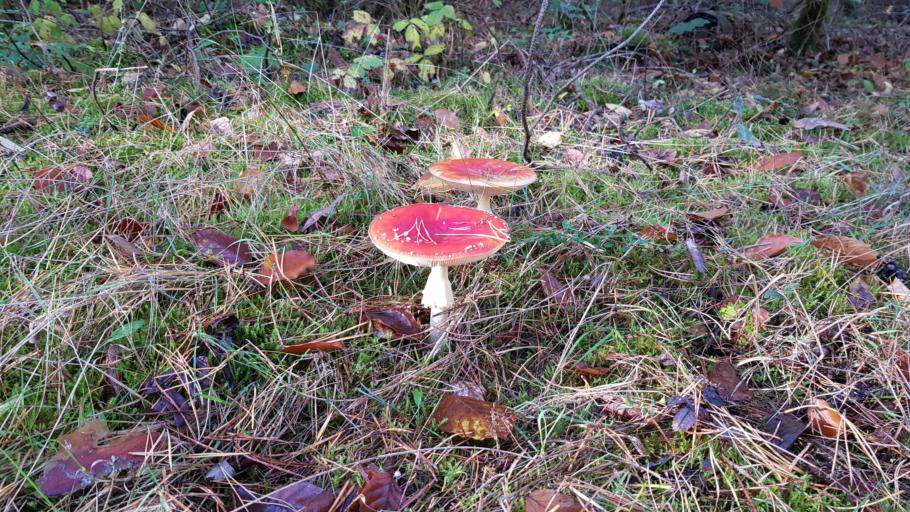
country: DE
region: Lower Saxony
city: Wendisch Evern
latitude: 53.2258
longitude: 10.4449
